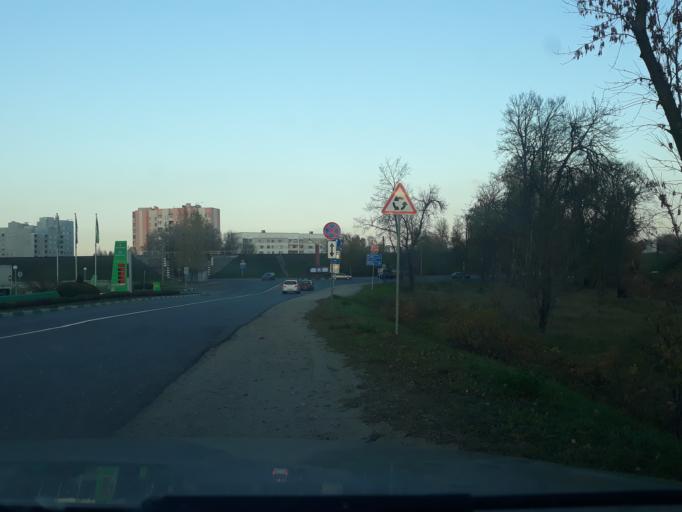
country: BY
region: Grodnenskaya
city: Vawkavysk
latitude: 53.1511
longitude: 24.4282
